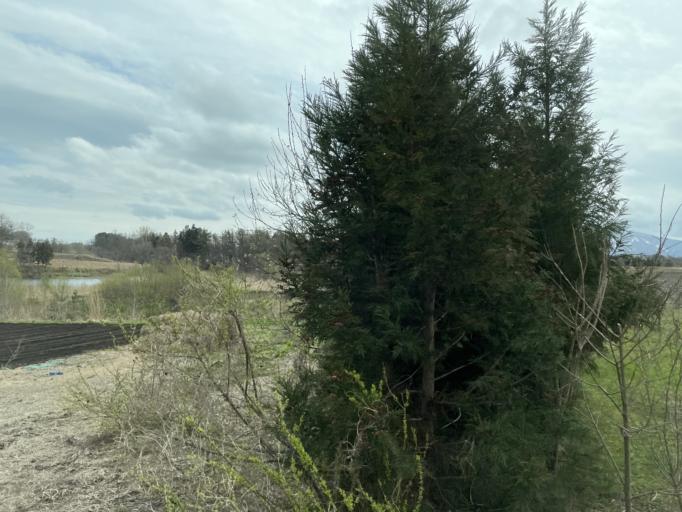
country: JP
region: Aomori
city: Shimokizukuri
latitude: 40.7852
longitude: 140.2902
